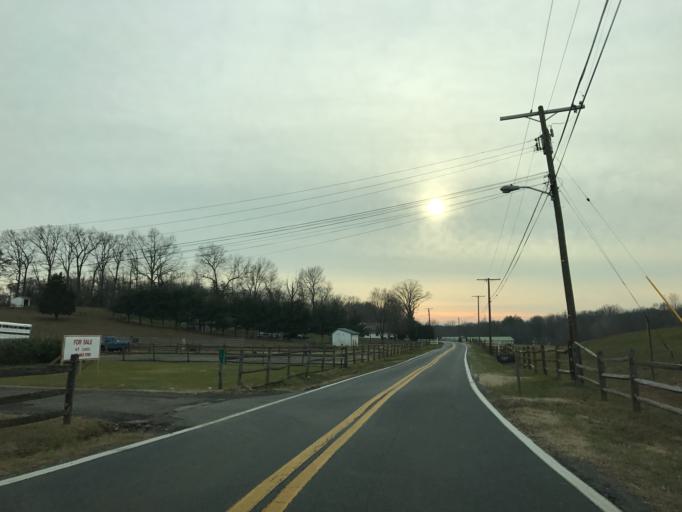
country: US
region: Maryland
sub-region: Baltimore County
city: White Marsh
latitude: 39.3990
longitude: -76.4091
